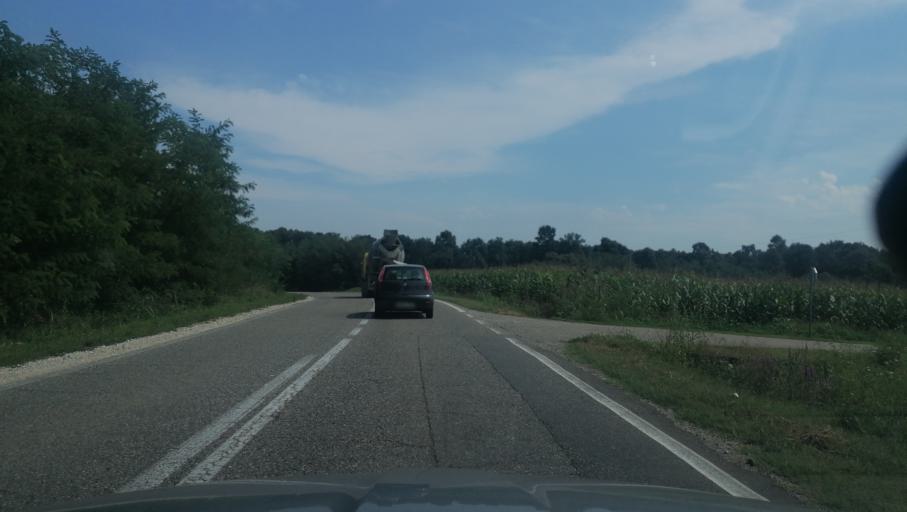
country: BA
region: Republika Srpska
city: Velika Obarska
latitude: 44.7794
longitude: 19.1049
